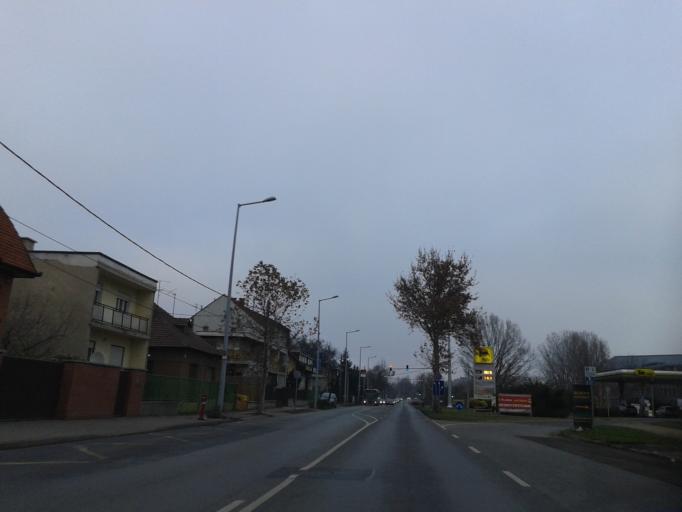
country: HU
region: Budapest
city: Budapest XIV. keruelet
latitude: 47.5259
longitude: 19.1202
